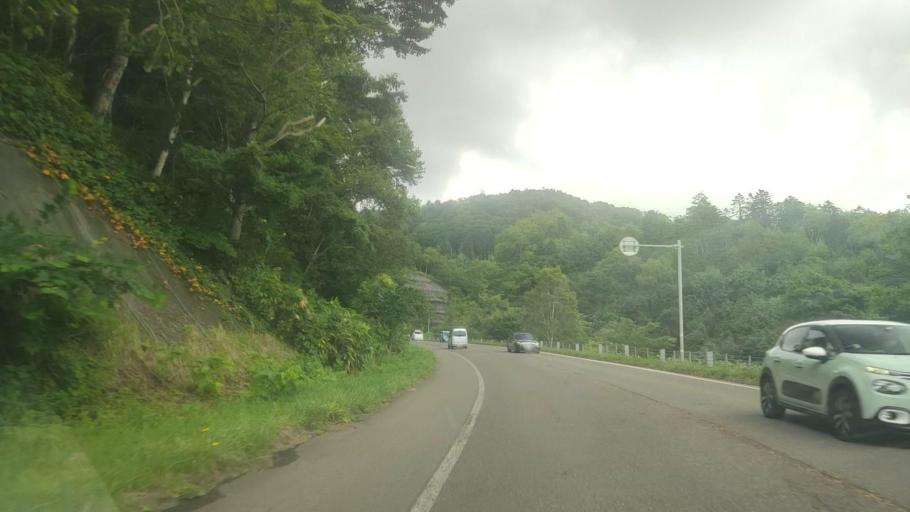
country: JP
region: Hokkaido
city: Niseko Town
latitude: 42.5985
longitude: 140.4671
